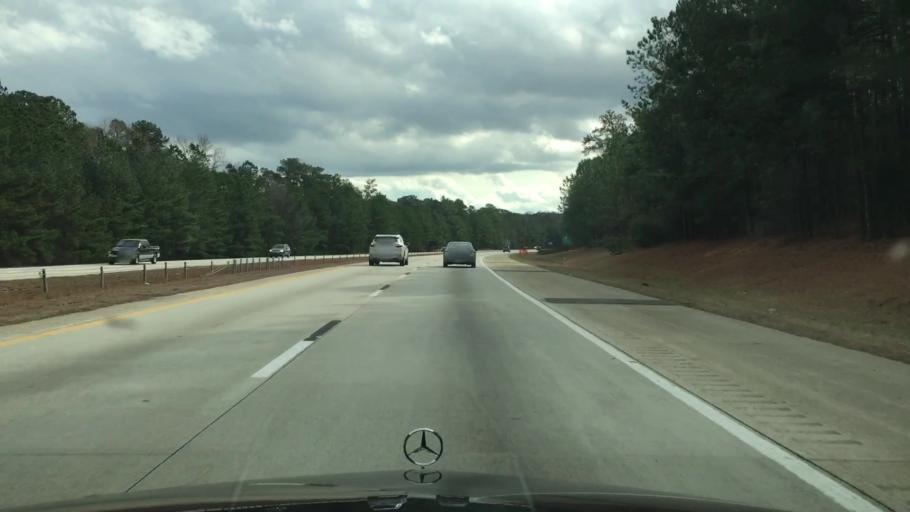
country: US
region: North Carolina
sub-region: Wake County
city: Garner
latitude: 35.6787
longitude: -78.5653
